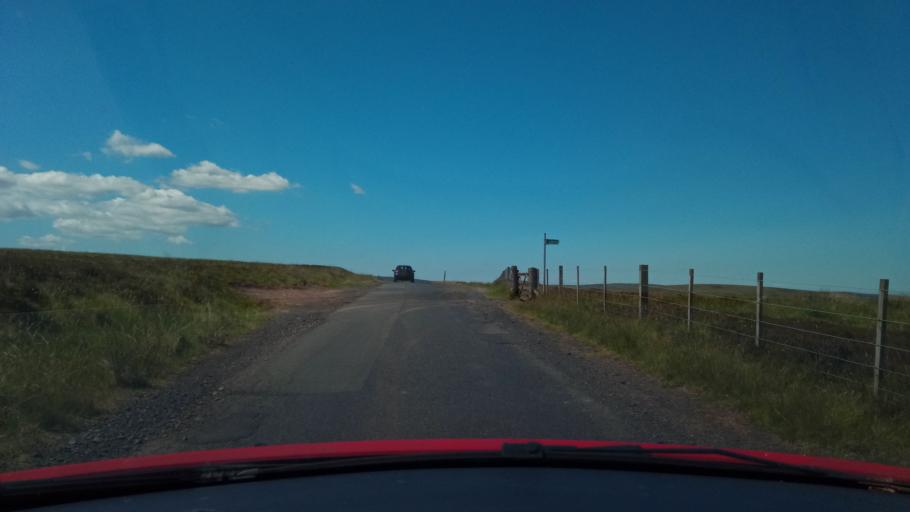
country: GB
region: Scotland
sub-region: East Lothian
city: Dunbar
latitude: 55.8404
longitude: -2.5583
